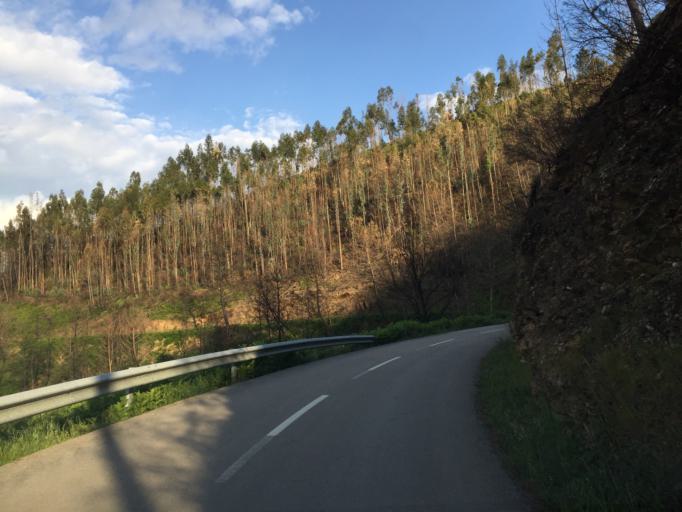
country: PT
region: Coimbra
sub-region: Arganil
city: Arganil
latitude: 40.1365
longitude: -8.0025
